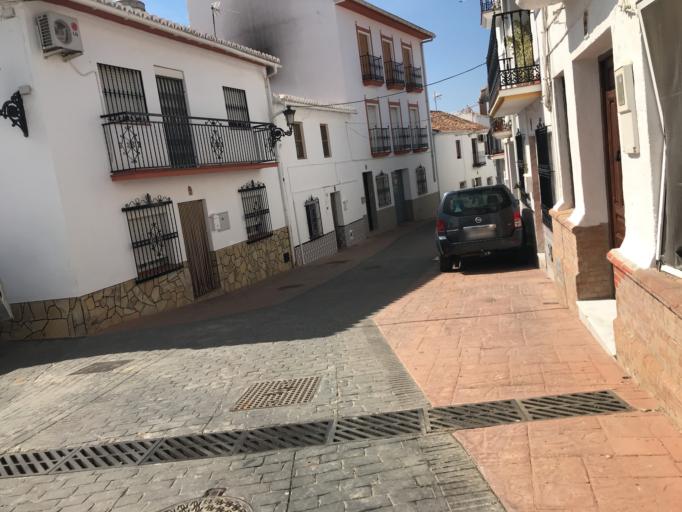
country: ES
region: Andalusia
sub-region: Provincia de Malaga
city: Periana
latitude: 36.9273
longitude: -4.1920
